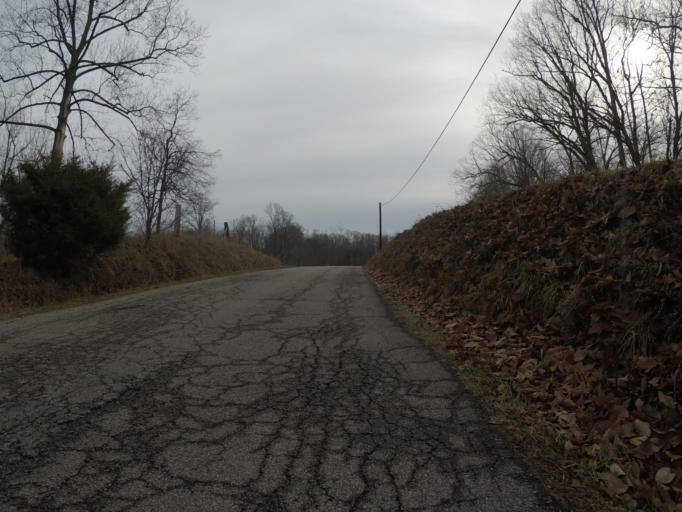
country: US
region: West Virginia
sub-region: Wayne County
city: Lavalette
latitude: 38.3550
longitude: -82.4108
